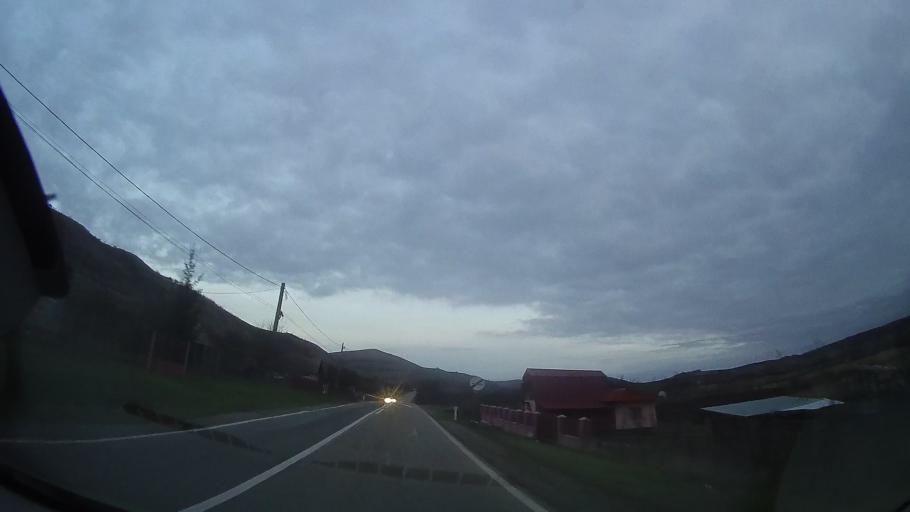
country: RO
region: Cluj
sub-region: Comuna Caianu
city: Caianu
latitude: 46.8006
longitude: 23.9404
